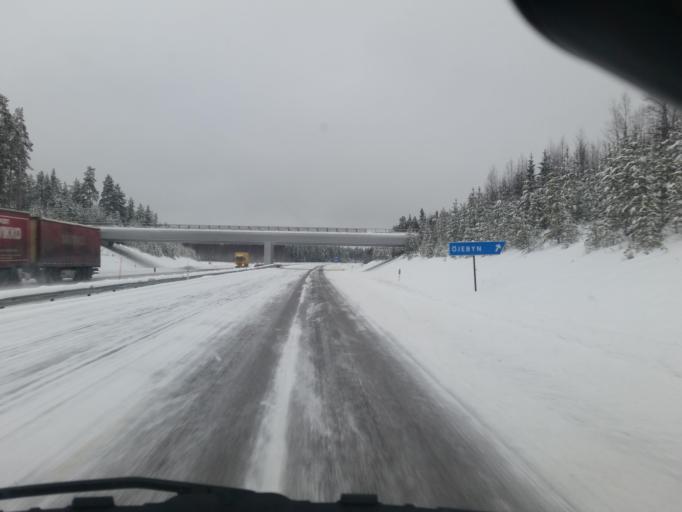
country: SE
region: Norrbotten
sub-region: Pitea Kommun
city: Norrfjarden
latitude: 65.3709
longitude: 21.4296
